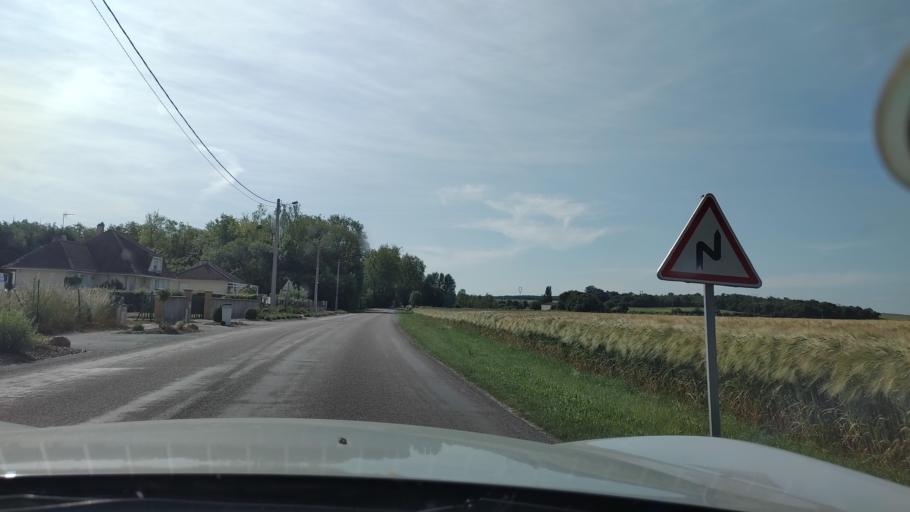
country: FR
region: Champagne-Ardenne
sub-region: Departement de l'Aube
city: Nogent-sur-Seine
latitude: 48.4716
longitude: 3.5613
